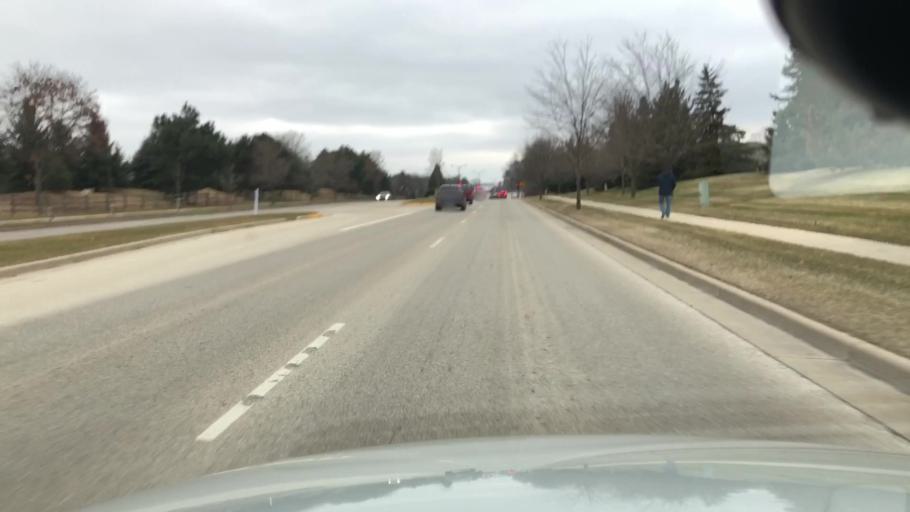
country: US
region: Wisconsin
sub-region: Waukesha County
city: Brookfield
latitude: 43.0414
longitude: -88.1269
